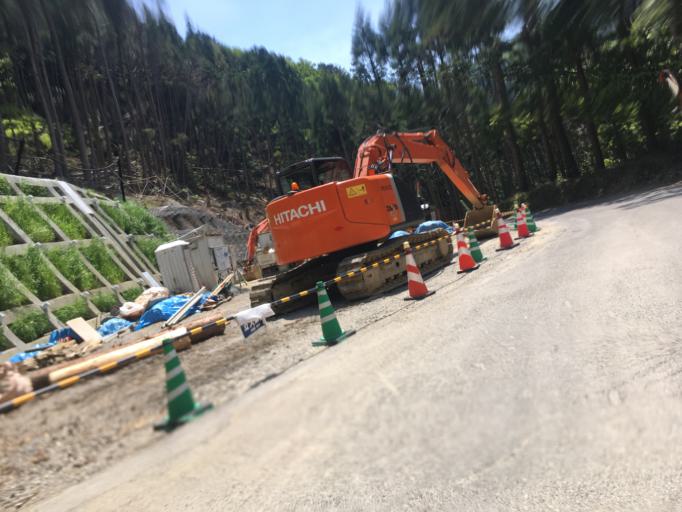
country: JP
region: Kyoto
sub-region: Kyoto-shi
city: Kamigyo-ku
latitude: 35.0946
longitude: 135.7428
